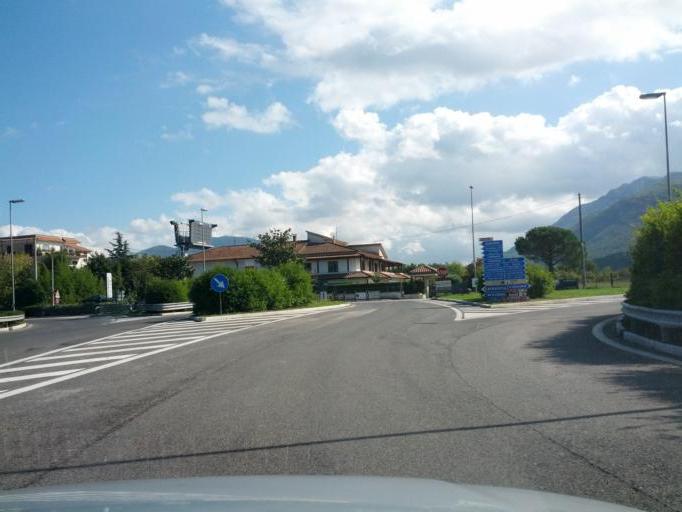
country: IT
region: Campania
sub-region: Provincia di Caserta
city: Bivio Mortola
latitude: 41.4330
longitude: 13.9021
